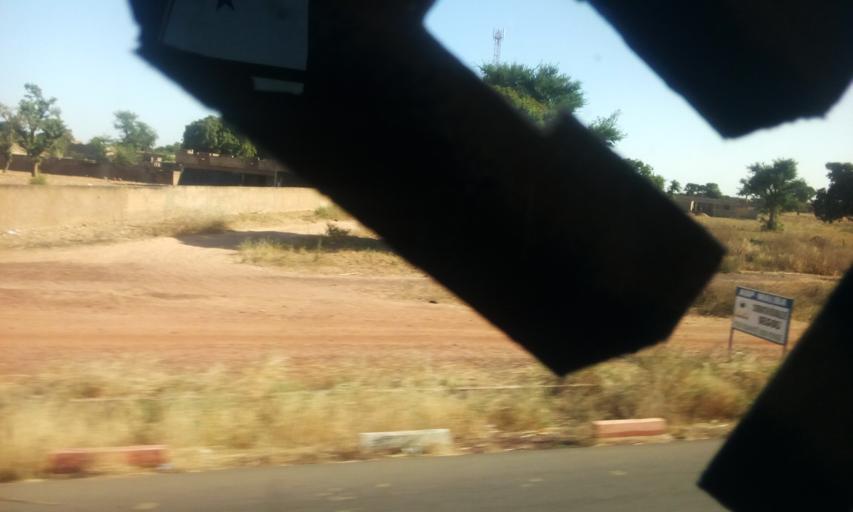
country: ML
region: Segou
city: Segou
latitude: 13.4129
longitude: -6.3247
